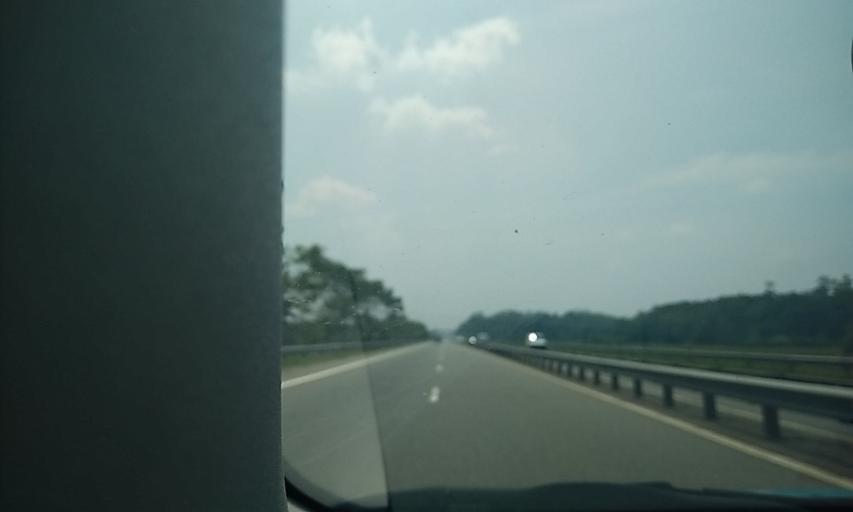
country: LK
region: Western
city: Horana South
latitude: 6.7429
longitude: 79.9980
